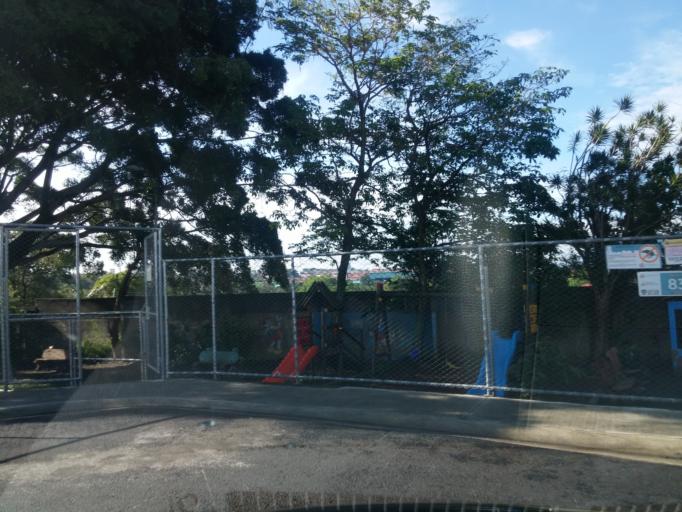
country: CR
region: Heredia
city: Mercedes
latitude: 10.0014
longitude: -84.1411
